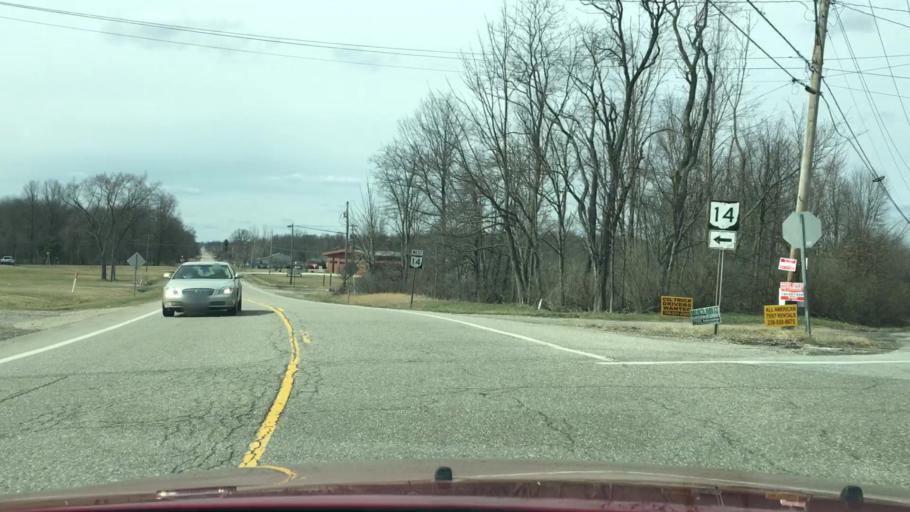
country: US
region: Ohio
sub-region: Mahoning County
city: Sebring
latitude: 41.0265
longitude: -81.0505
